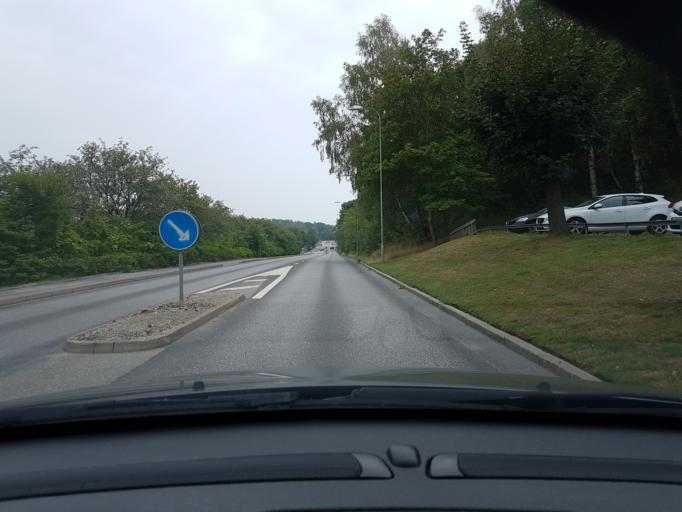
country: SE
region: Vaestra Goetaland
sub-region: Goteborg
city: Majorna
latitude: 57.6432
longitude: 11.8948
